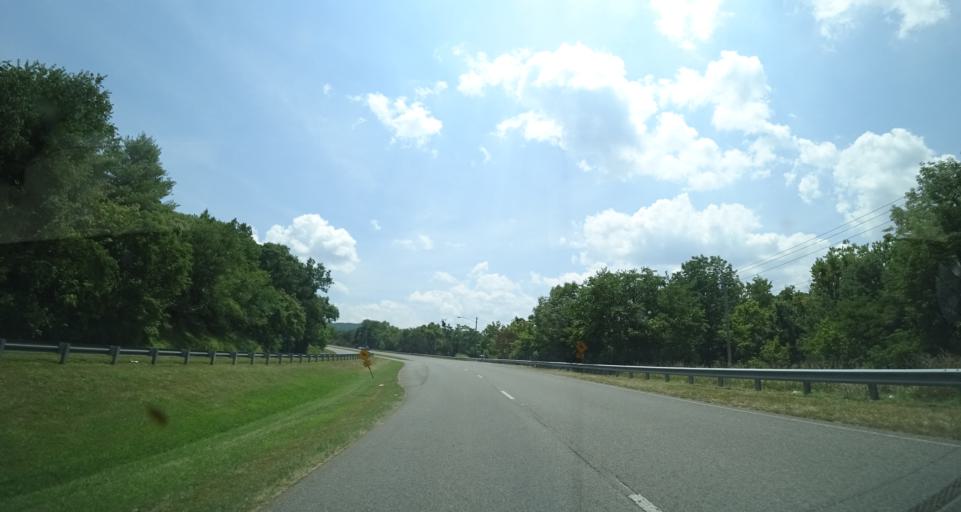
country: US
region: Virginia
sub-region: City of Radford
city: Radford
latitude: 37.0991
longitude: -80.5827
